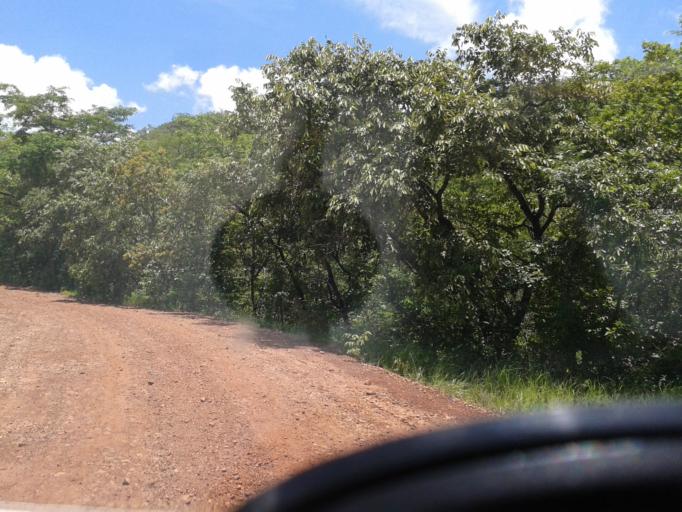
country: BR
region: Minas Gerais
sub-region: Santa Vitoria
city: Santa Vitoria
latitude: -18.9850
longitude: -49.8968
